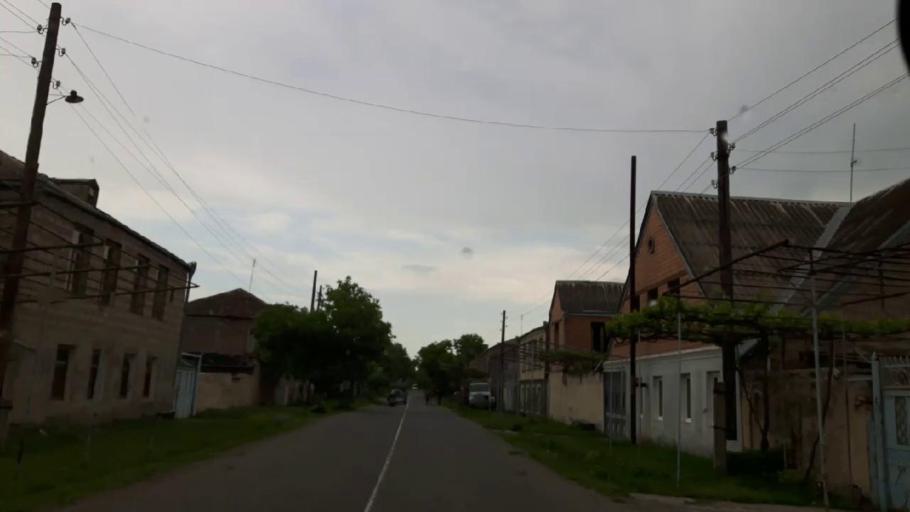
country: GE
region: Shida Kartli
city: Gori
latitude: 41.9604
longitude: 44.2053
